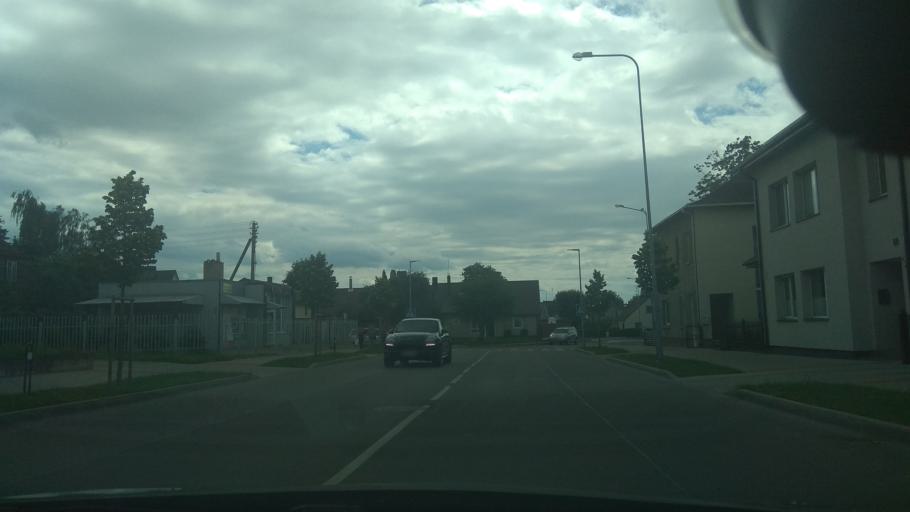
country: LT
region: Marijampoles apskritis
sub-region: Marijampole Municipality
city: Marijampole
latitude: 54.5520
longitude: 23.3535
